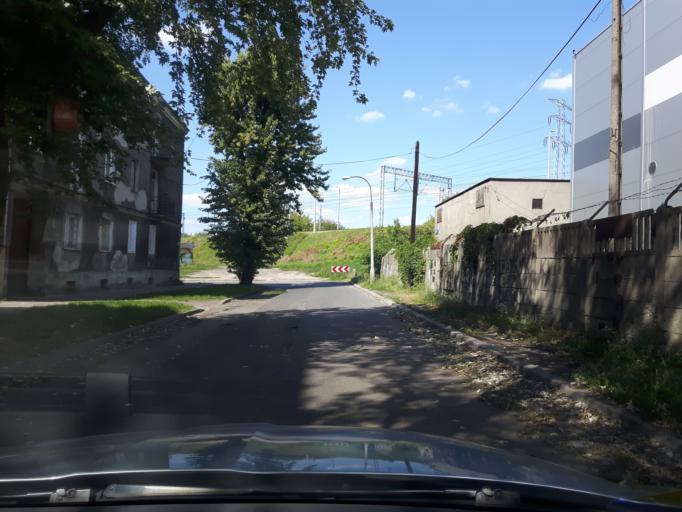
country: PL
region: Masovian Voivodeship
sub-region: Warszawa
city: Praga Polnoc
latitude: 52.2615
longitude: 21.0594
